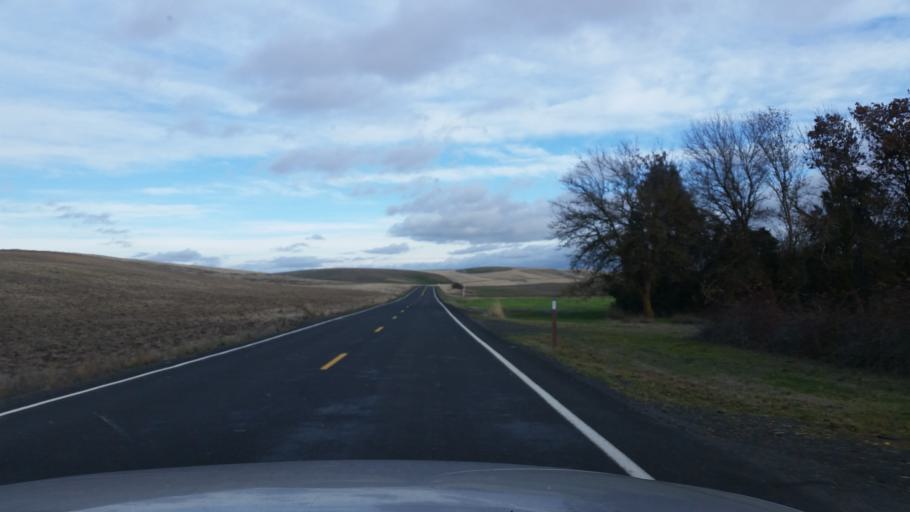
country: US
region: Washington
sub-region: Lincoln County
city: Davenport
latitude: 47.3562
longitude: -118.0550
